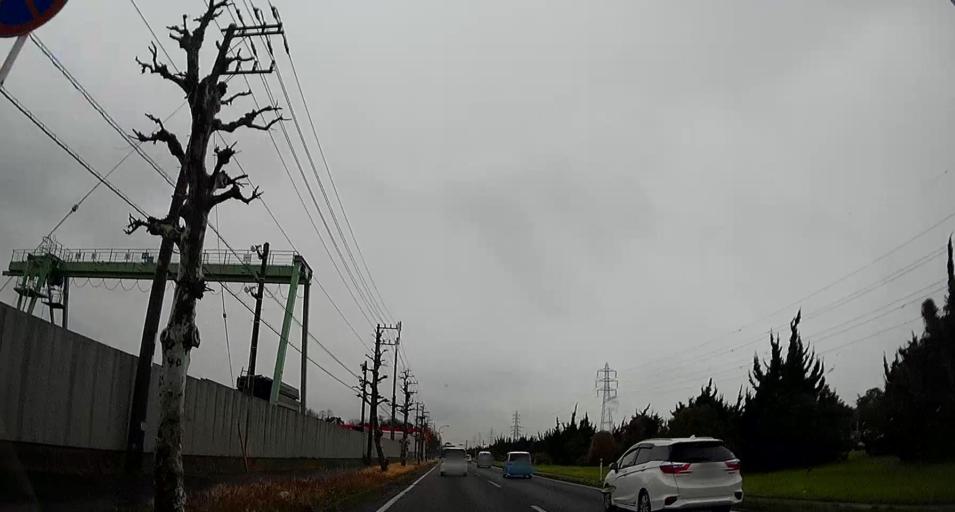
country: JP
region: Chiba
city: Ichihara
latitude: 35.5137
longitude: 140.0577
